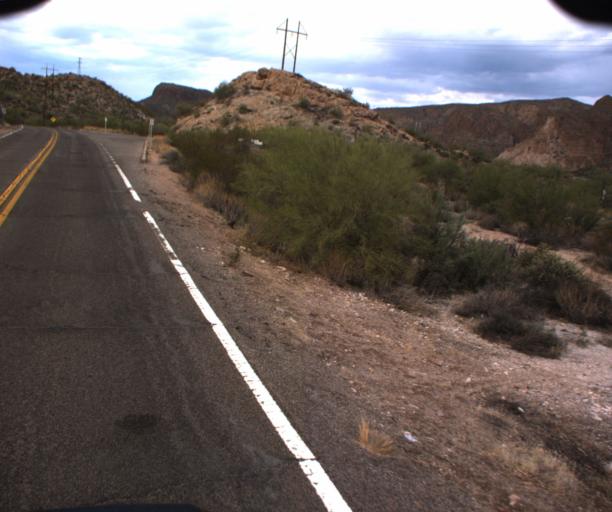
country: US
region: Arizona
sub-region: Pinal County
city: Apache Junction
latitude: 33.5334
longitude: -111.4283
